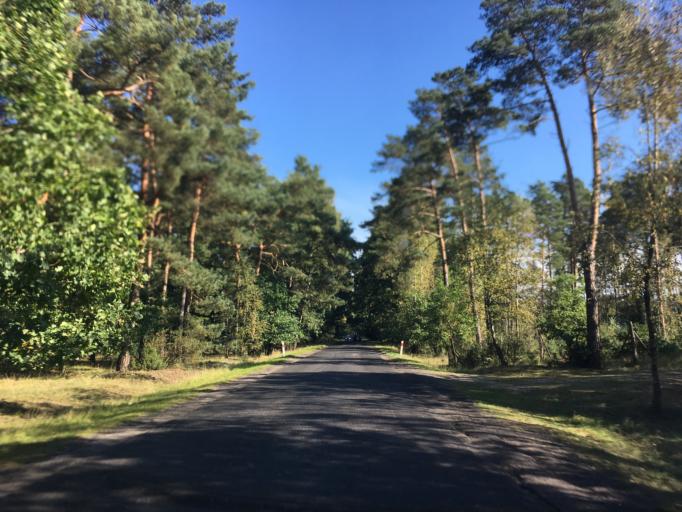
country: PL
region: Kujawsko-Pomorskie
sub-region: Powiat swiecki
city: Warlubie
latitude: 53.5986
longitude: 18.5740
